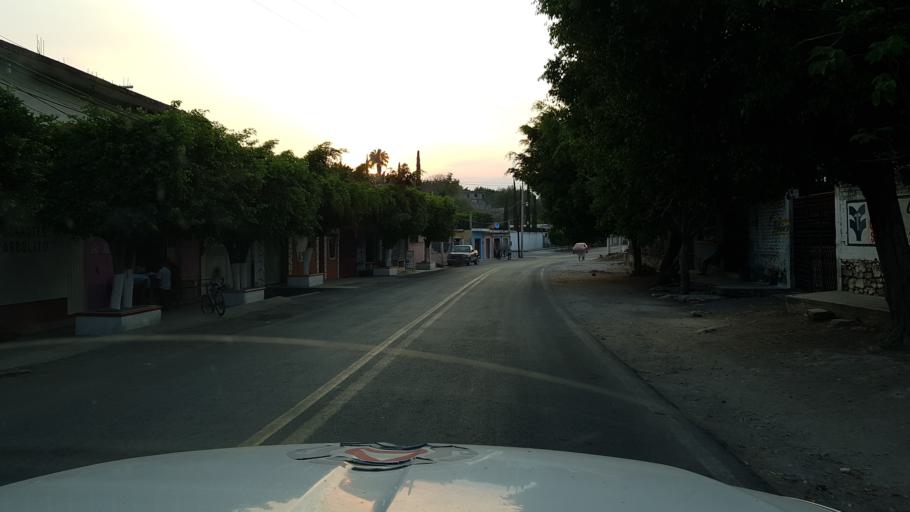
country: MX
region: Morelos
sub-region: Ayala
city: Abelardo L. Rodriguez
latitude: 18.7253
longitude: -98.9976
